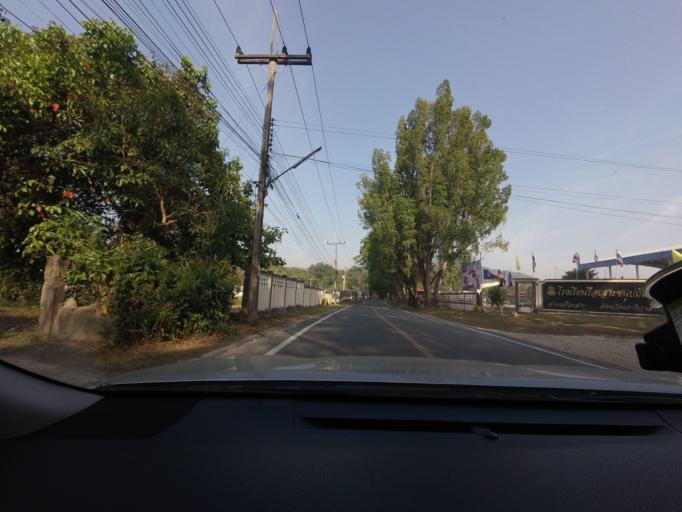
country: TH
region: Narathiwat
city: Rueso
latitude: 6.3989
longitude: 101.5248
